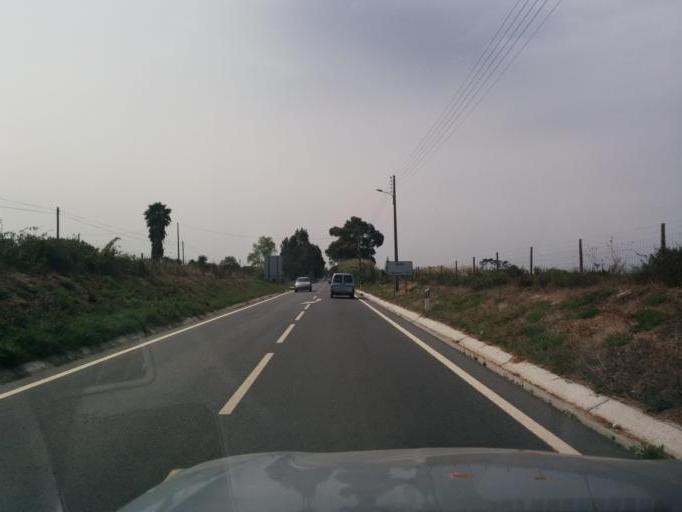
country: PT
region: Beja
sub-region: Odemira
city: Vila Nova de Milfontes
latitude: 37.6529
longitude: -8.7595
